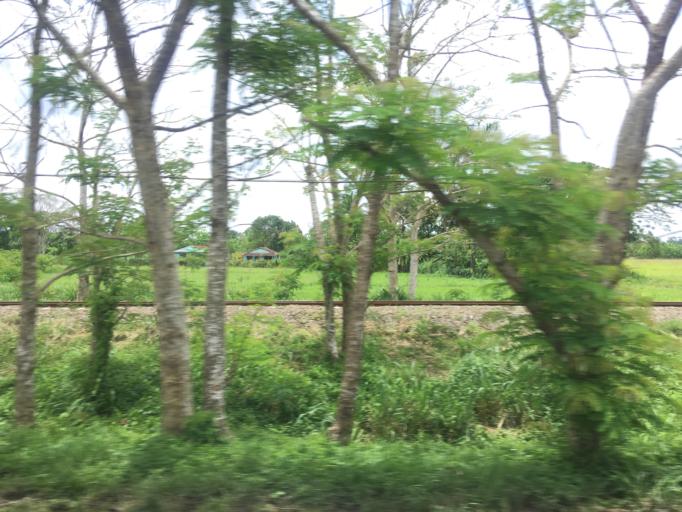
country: CU
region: Villa Clara
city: Esperanza
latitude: 22.4335
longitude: -80.0666
